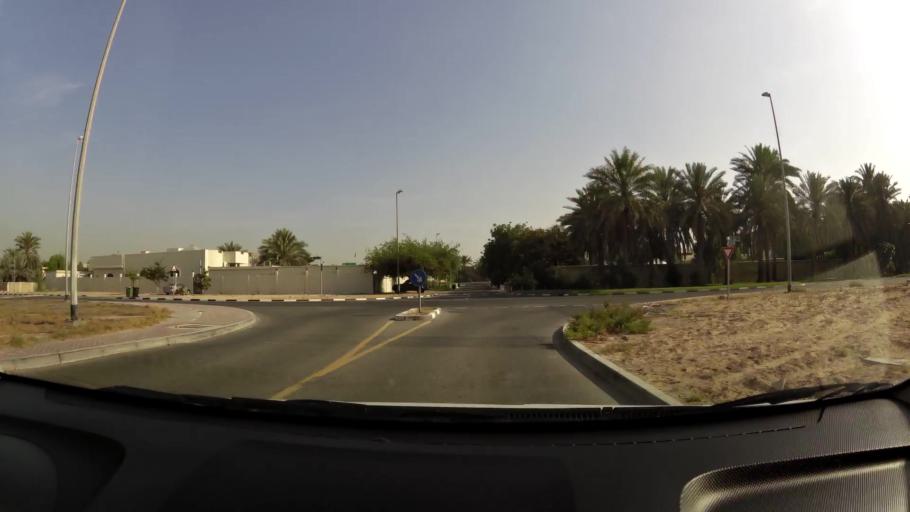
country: AE
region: Ash Shariqah
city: Sharjah
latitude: 25.2485
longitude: 55.4106
